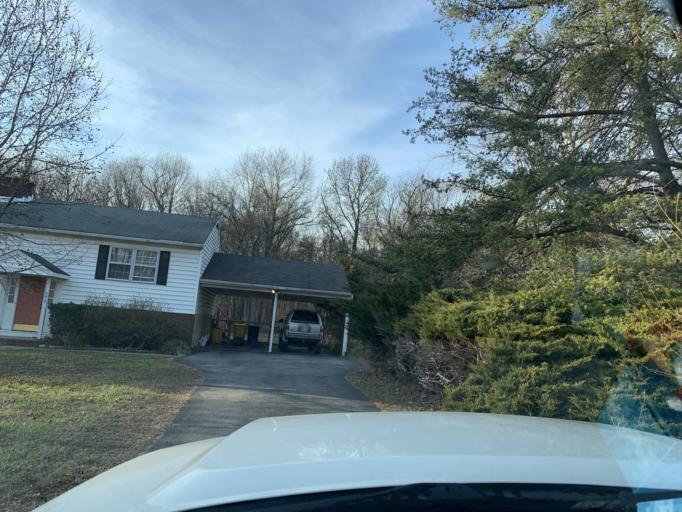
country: US
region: Maryland
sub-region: Anne Arundel County
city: Fort Meade
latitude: 39.1366
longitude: -76.7472
